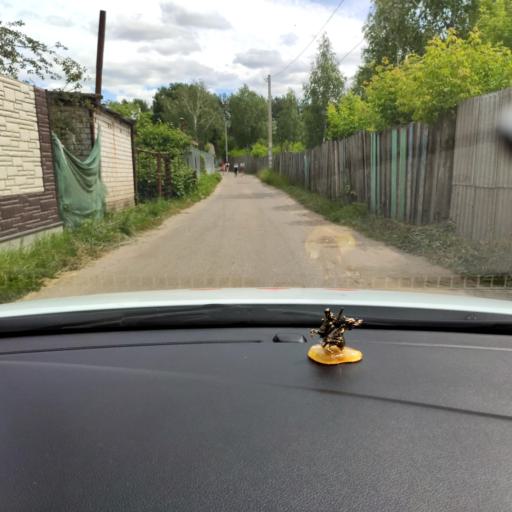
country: RU
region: Tatarstan
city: Staroye Arakchino
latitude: 55.8900
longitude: 49.0424
